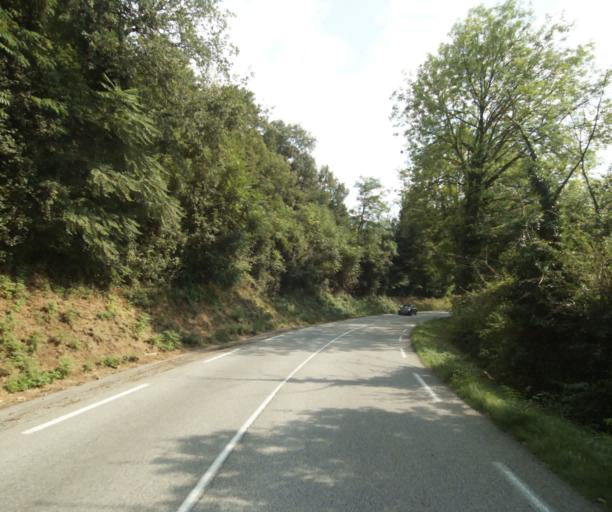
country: FR
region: Rhone-Alpes
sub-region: Departement de l'Isere
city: Vizille
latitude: 45.0895
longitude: 5.7799
